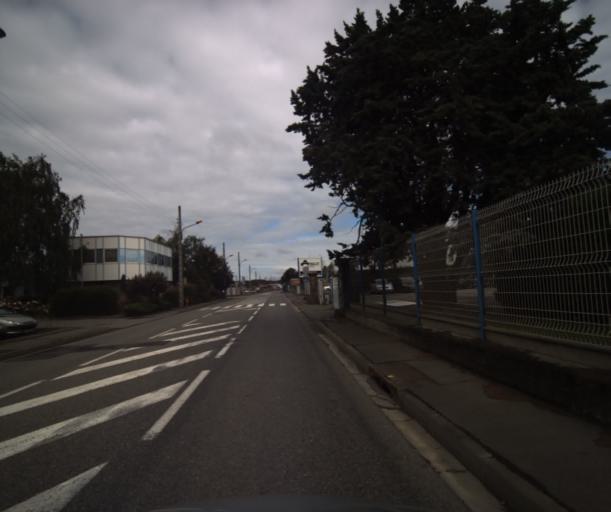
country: FR
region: Midi-Pyrenees
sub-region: Departement de la Haute-Garonne
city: Portet-sur-Garonne
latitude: 43.5501
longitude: 1.4131
